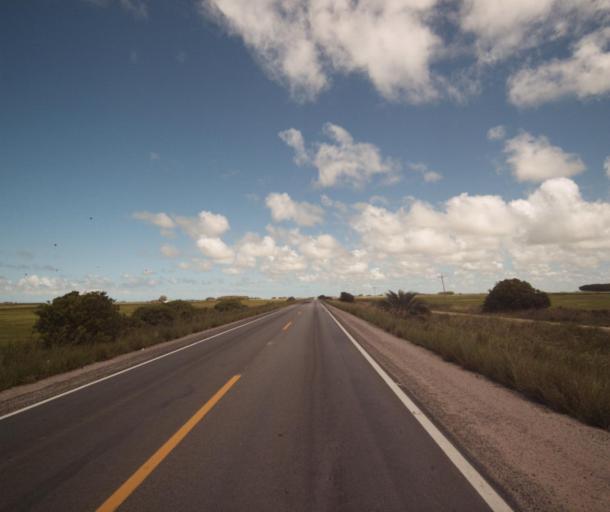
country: UY
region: Cerro Largo
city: Rio Branco
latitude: -32.8912
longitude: -52.7244
